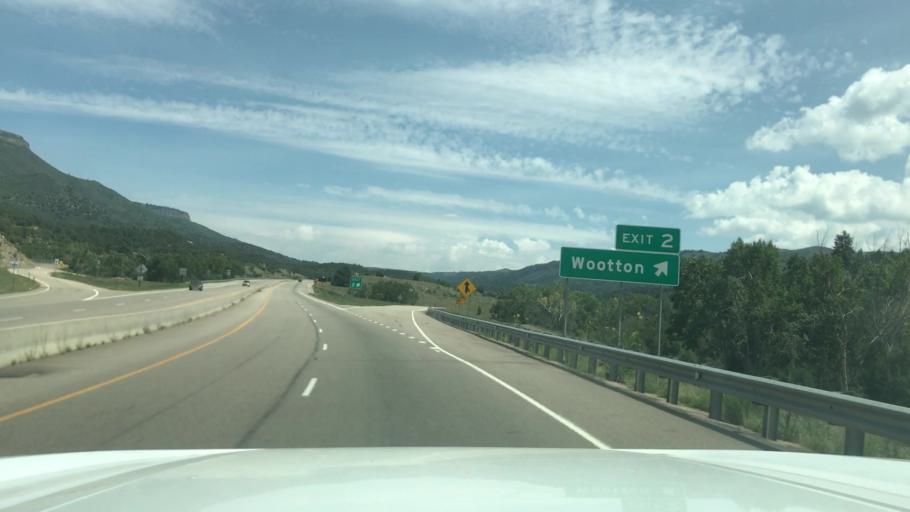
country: US
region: New Mexico
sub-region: Colfax County
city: Raton
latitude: 37.0215
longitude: -104.4953
